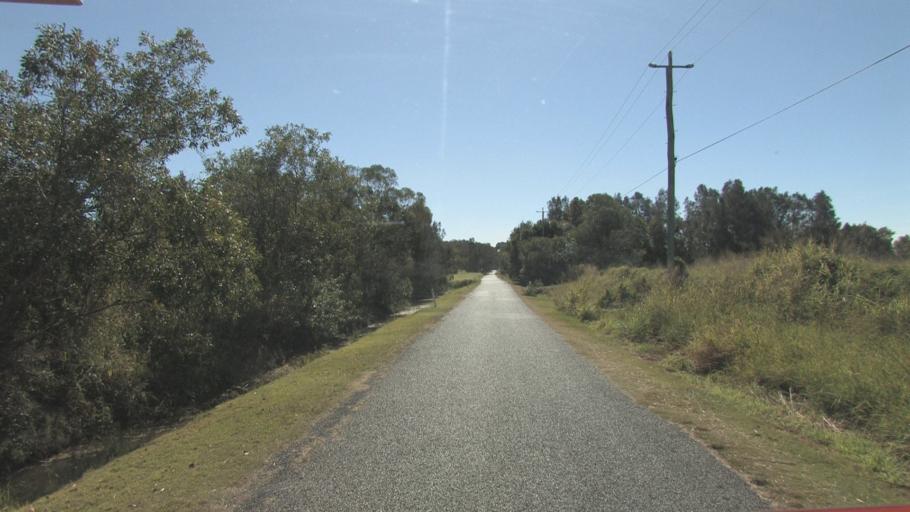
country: AU
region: Queensland
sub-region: Gold Coast
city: Yatala
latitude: -27.6957
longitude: 153.2270
